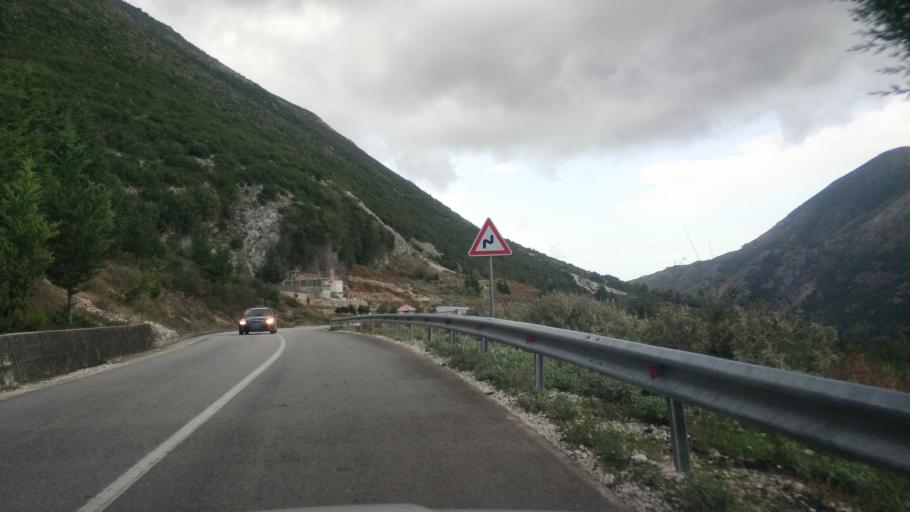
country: AL
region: Vlore
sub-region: Rrethi i Vlores
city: Orikum
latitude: 40.2374
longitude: 19.5530
